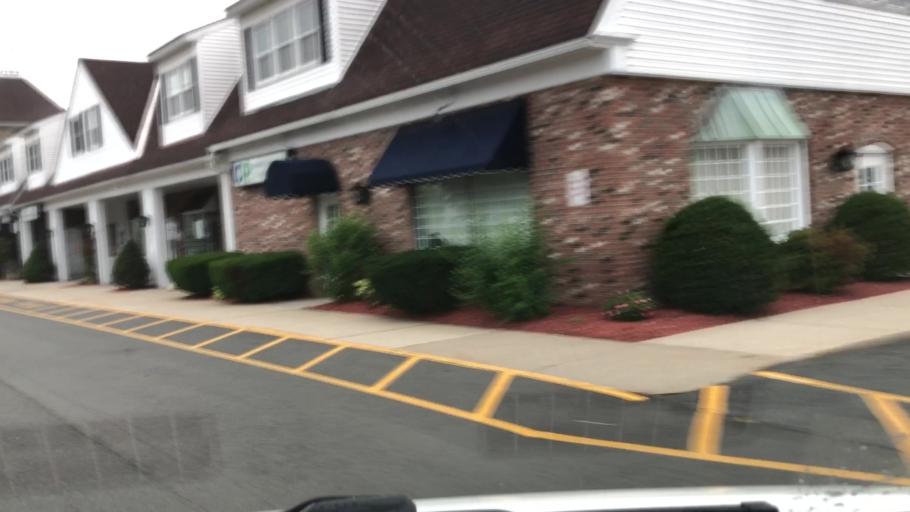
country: US
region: Massachusetts
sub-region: Hampshire County
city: Northampton
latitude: 42.3301
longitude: -72.6335
